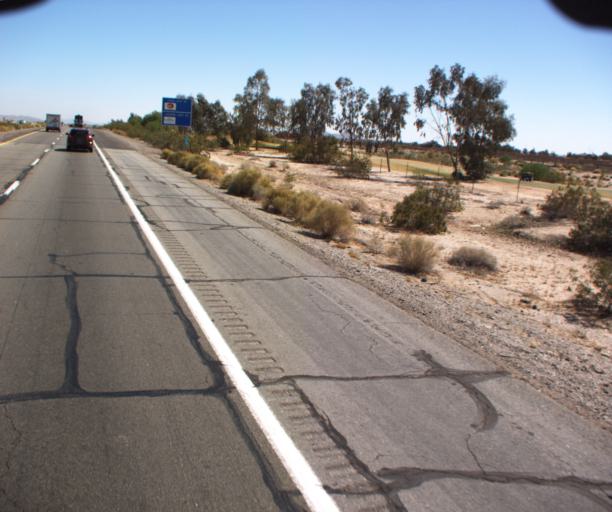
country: US
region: Arizona
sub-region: Yuma County
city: Wellton
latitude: 32.6545
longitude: -114.1726
